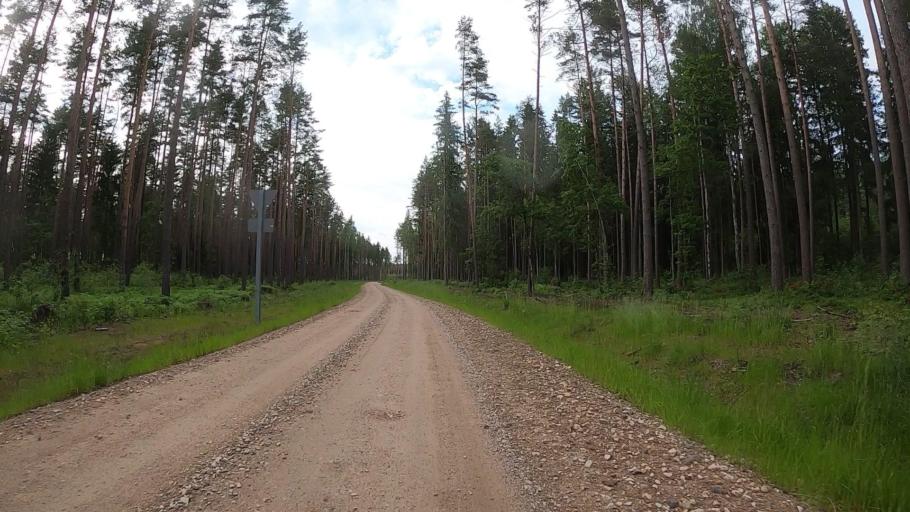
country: LV
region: Olaine
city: Olaine
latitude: 56.7645
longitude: 23.9033
